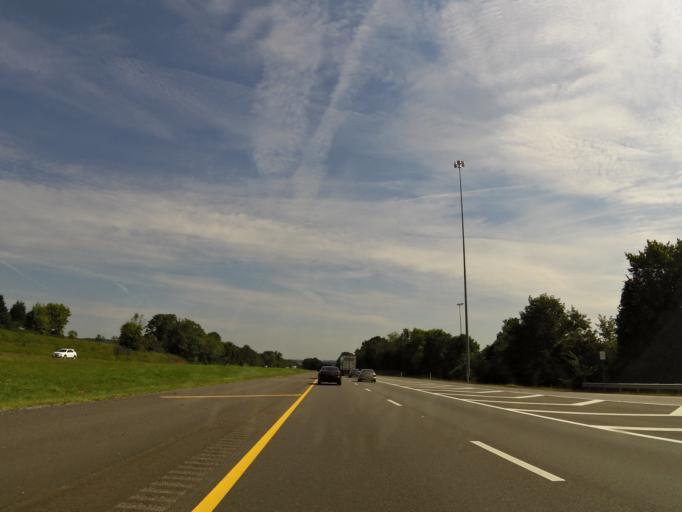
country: US
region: Tennessee
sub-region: Jefferson County
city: White Pine
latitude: 36.1112
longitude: -83.3339
